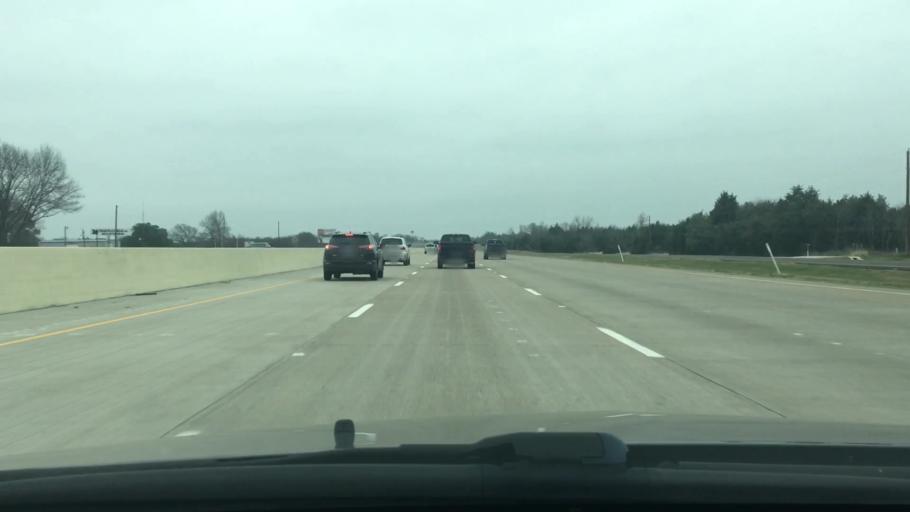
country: US
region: Texas
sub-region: Navarro County
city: Corsicana
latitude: 32.0047
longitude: -96.4323
